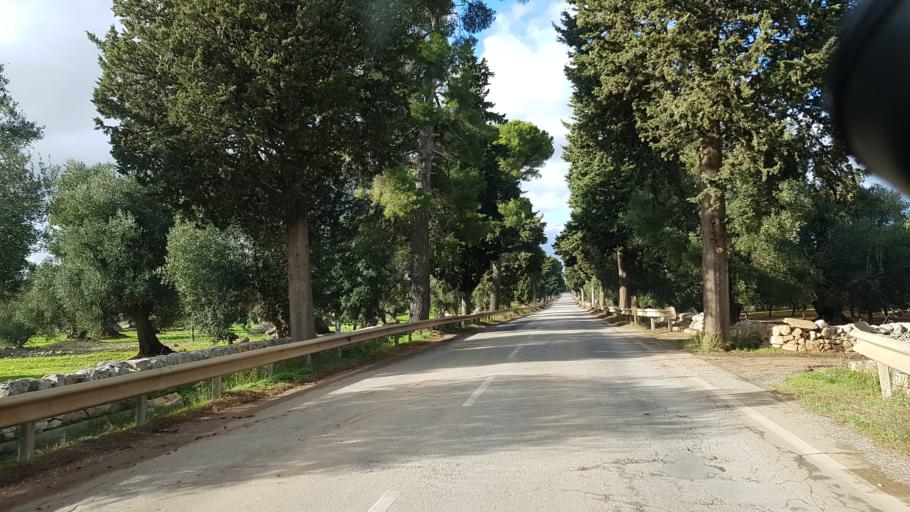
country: IT
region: Apulia
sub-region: Provincia di Brindisi
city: Ostuni
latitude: 40.7548
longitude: 17.5415
